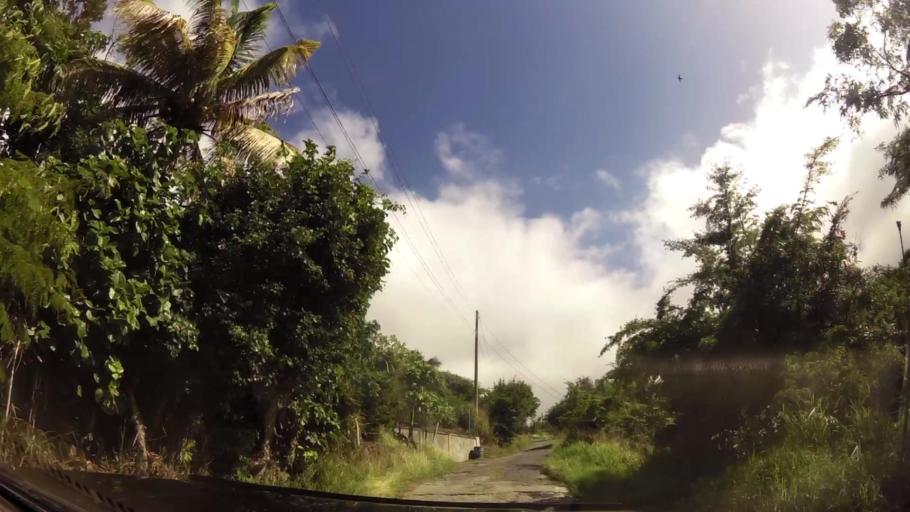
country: MS
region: Saint Peter
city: Brades
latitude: 16.7865
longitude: -62.2107
